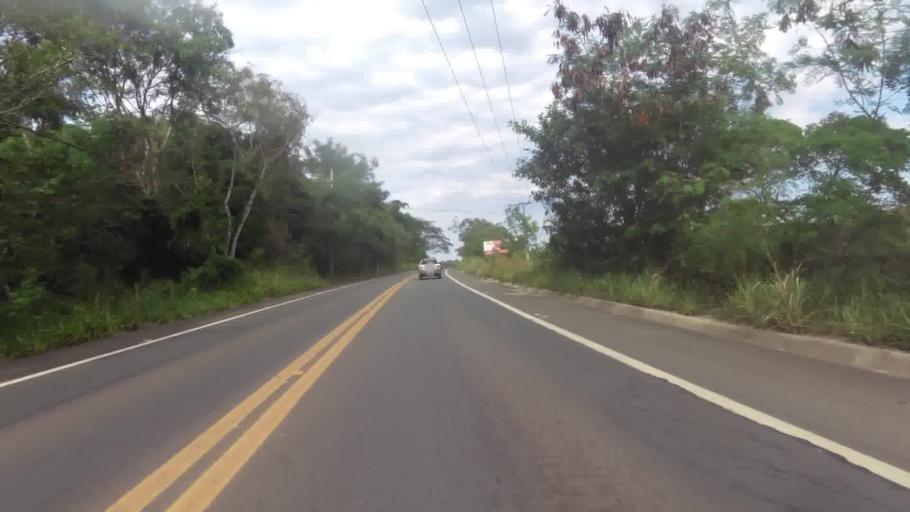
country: BR
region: Espirito Santo
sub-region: Piuma
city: Piuma
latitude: -20.8209
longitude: -40.6940
